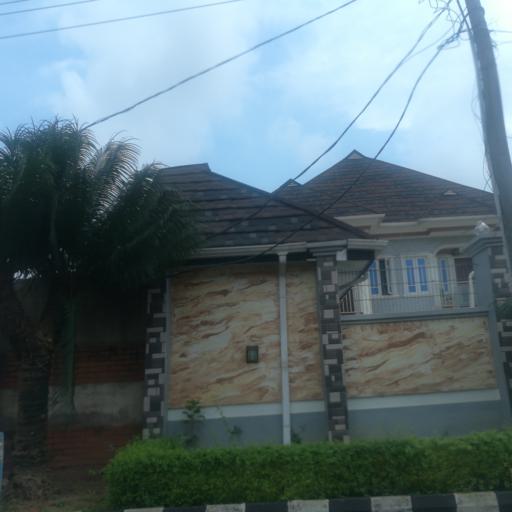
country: NG
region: Lagos
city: Ojota
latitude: 6.5764
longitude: 3.3940
